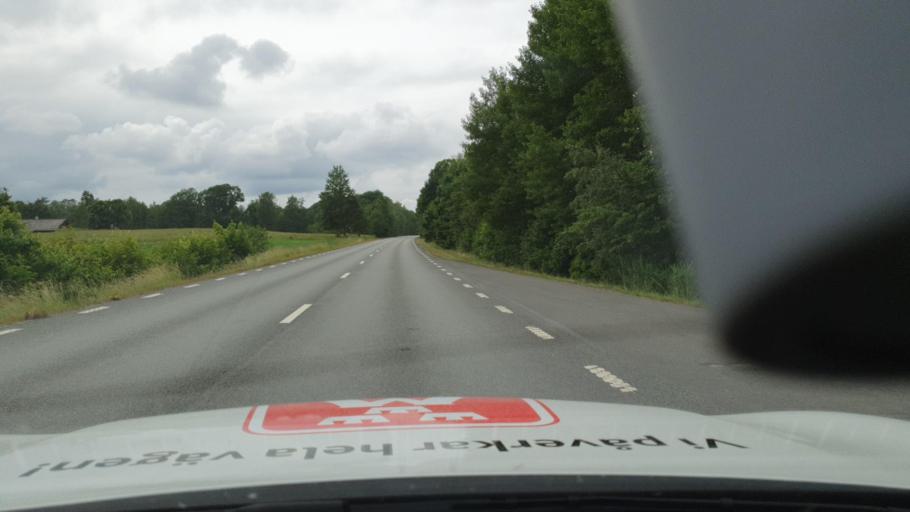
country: SE
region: Vaestra Goetaland
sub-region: Hjo Kommun
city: Hjo
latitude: 58.2264
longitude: 14.1838
